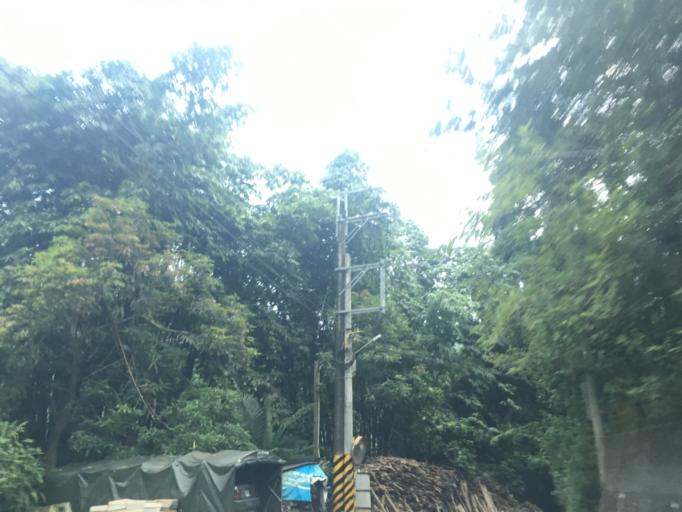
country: TW
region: Taiwan
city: Fengyuan
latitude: 24.1914
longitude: 120.7611
